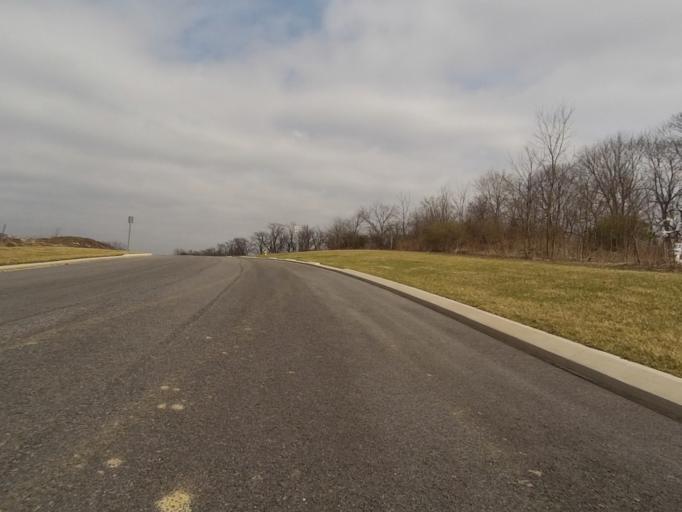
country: US
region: Pennsylvania
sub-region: Centre County
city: Boalsburg
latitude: 40.7877
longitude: -77.8094
